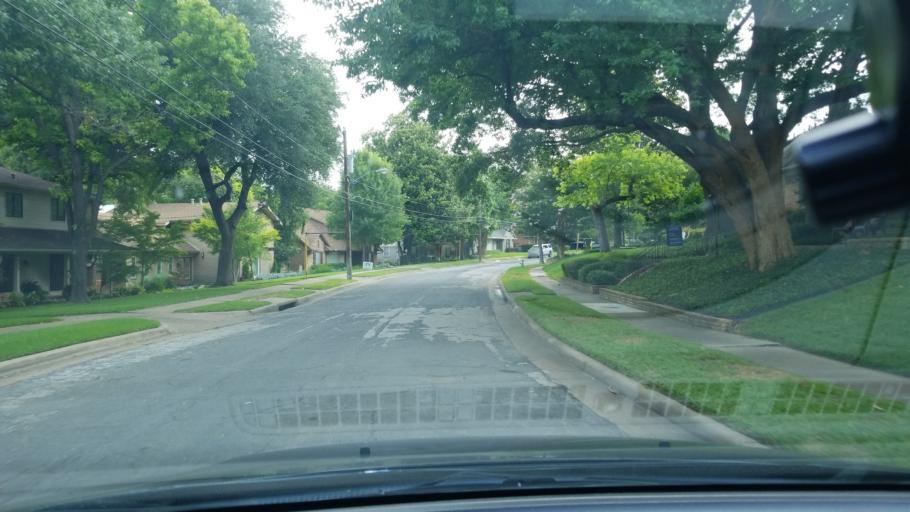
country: US
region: Texas
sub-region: Dallas County
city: Highland Park
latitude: 32.8199
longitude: -96.6967
